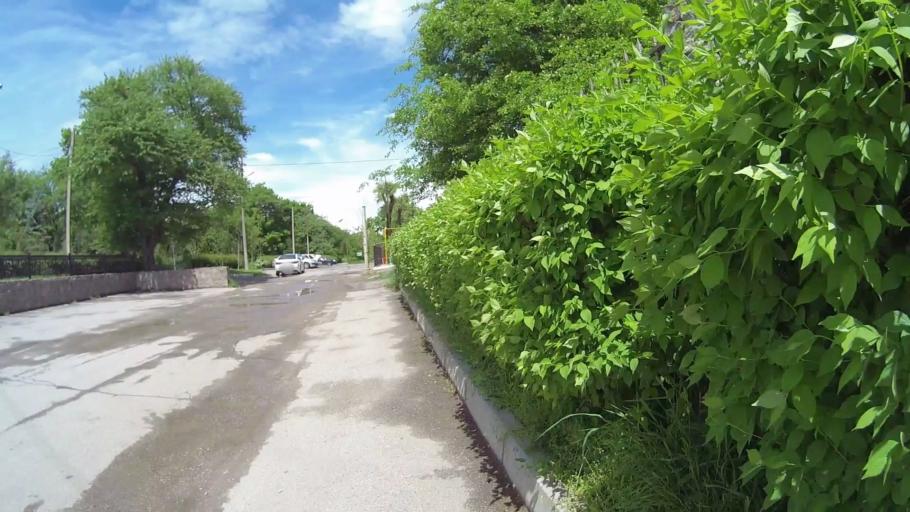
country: RU
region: Kabardino-Balkariya
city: Vol'nyy Aul
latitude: 43.4599
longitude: 43.5895
